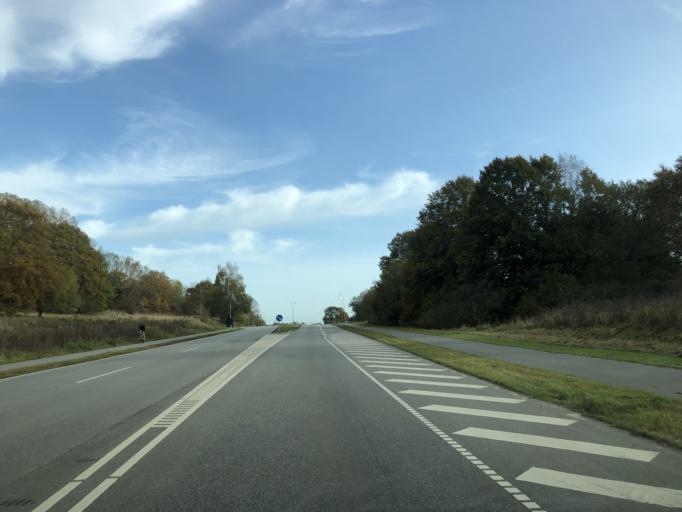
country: DK
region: Capital Region
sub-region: Allerod Kommune
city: Blovstrod
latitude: 55.8590
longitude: 12.4002
